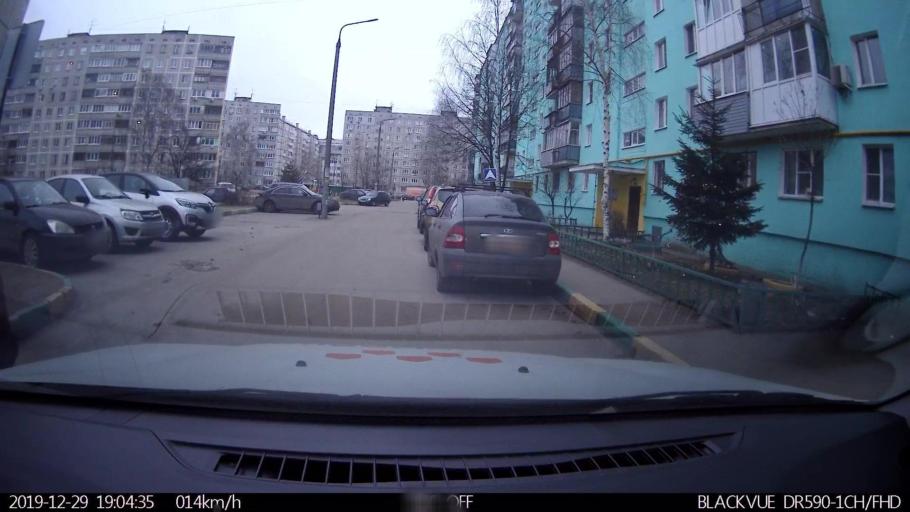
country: RU
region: Nizjnij Novgorod
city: Neklyudovo
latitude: 56.3573
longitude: 43.8580
